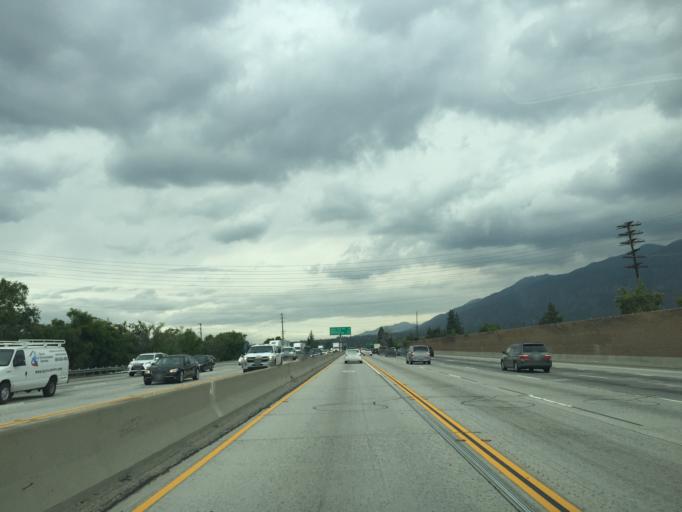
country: US
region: California
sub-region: Los Angeles County
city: Arcadia
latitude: 34.1437
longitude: -118.0224
